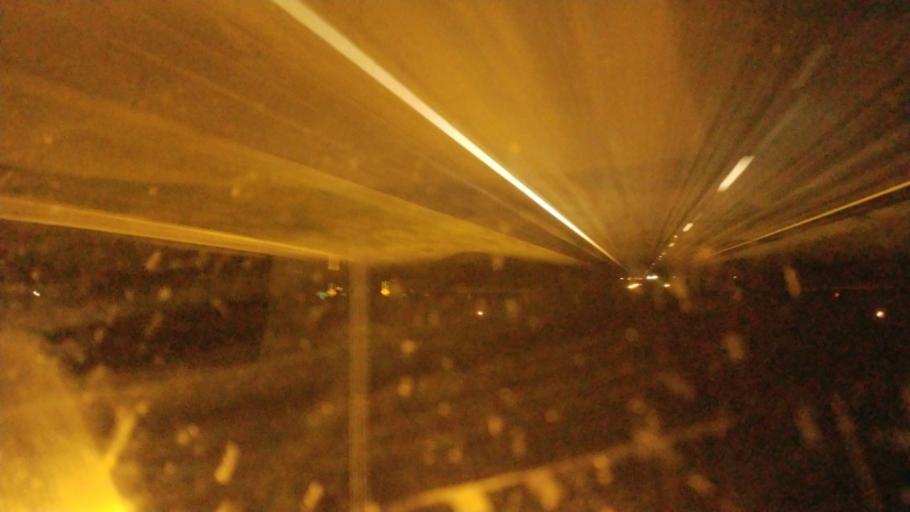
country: US
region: Ohio
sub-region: Hardin County
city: Ada
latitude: 40.8275
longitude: -83.8194
